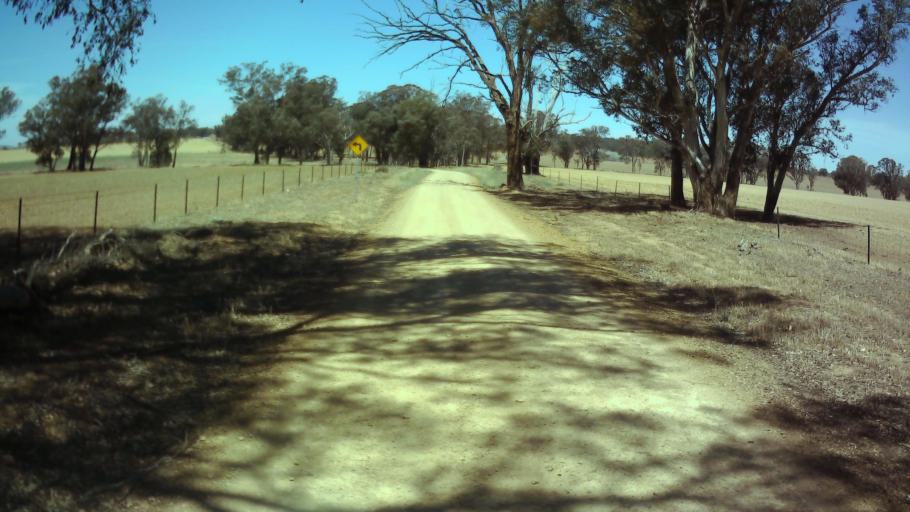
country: AU
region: New South Wales
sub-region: Weddin
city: Grenfell
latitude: -33.9220
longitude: 148.2104
